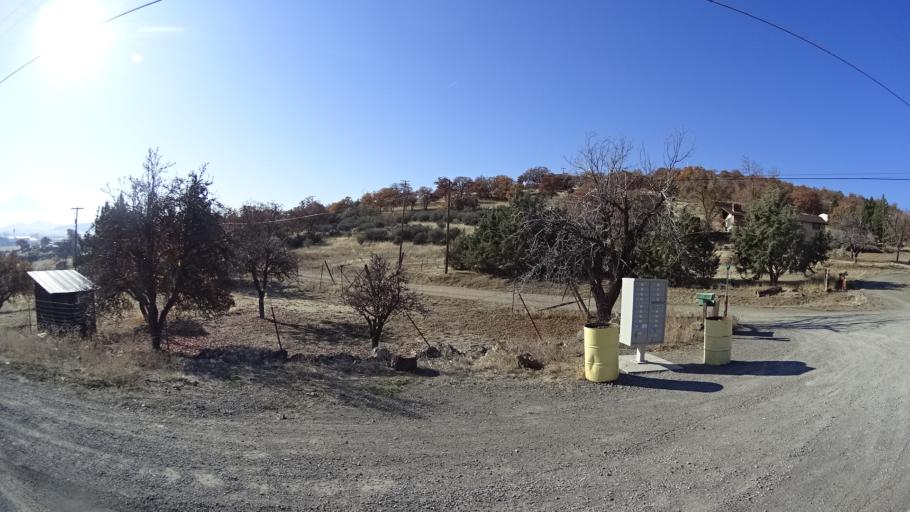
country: US
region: California
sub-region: Siskiyou County
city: Yreka
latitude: 41.7383
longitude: -122.6060
